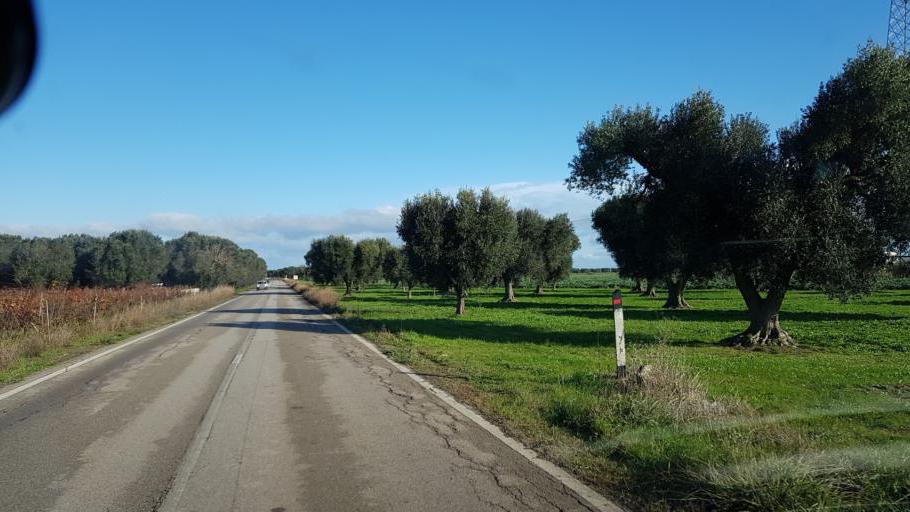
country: IT
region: Apulia
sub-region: Provincia di Brindisi
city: Tuturano
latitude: 40.5593
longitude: 17.9478
